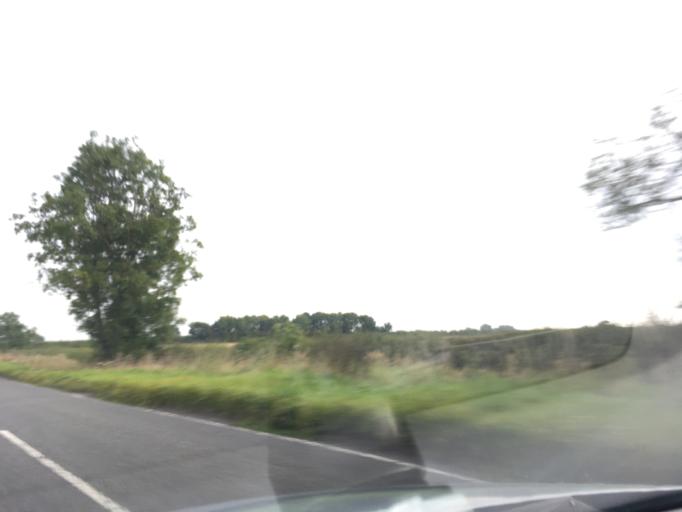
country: GB
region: England
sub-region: Oxfordshire
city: Kidlington
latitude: 51.8324
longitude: -1.2455
